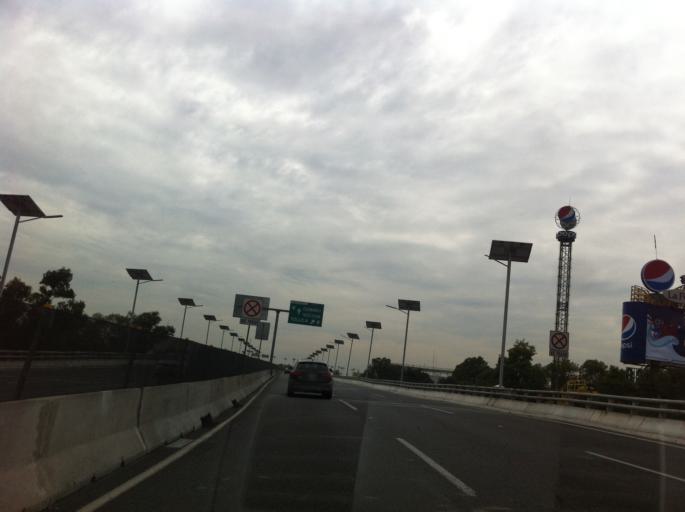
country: MX
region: Mexico City
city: Polanco
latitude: 19.4182
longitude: -99.1954
